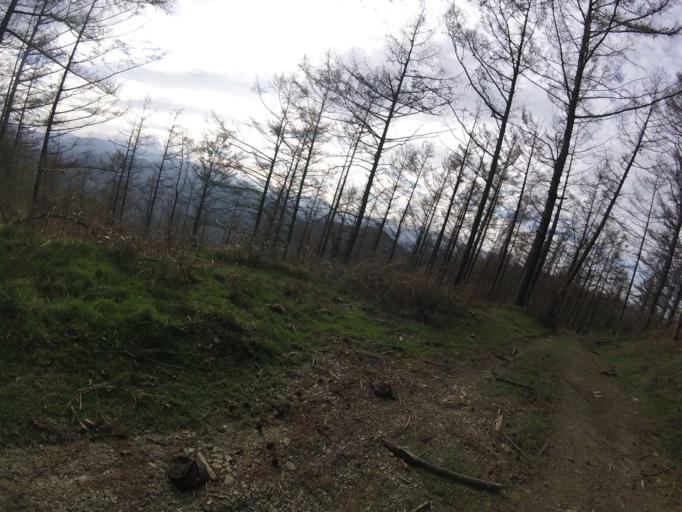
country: ES
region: Navarre
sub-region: Provincia de Navarra
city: Arano
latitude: 43.2418
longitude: -1.8556
